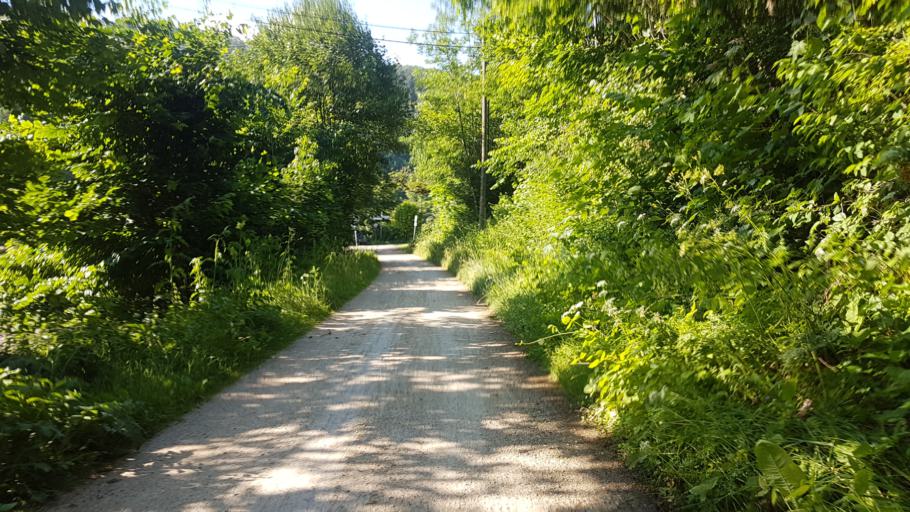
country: DE
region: Baden-Wuerttemberg
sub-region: Tuebingen Region
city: Stetten am Kalten Markt
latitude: 48.0894
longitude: 9.1019
